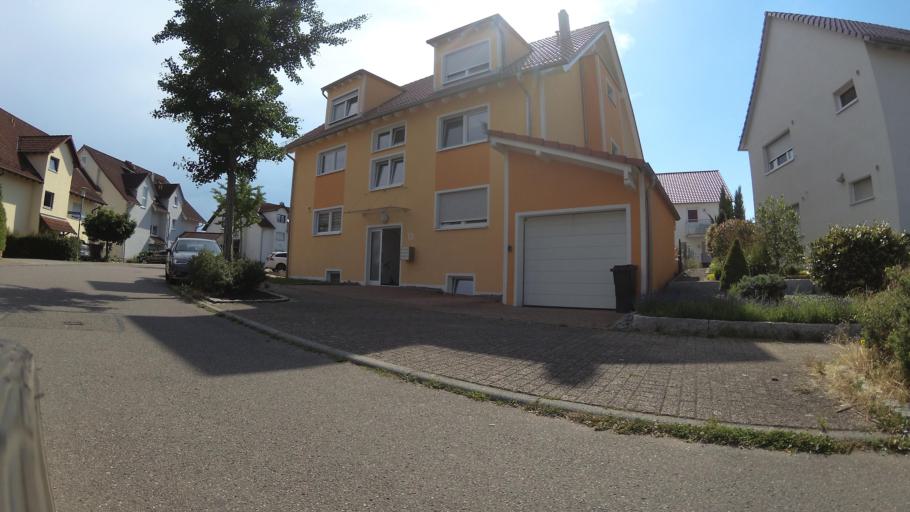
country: DE
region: Baden-Wuerttemberg
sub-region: Regierungsbezirk Stuttgart
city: Bad Rappenau
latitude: 49.2502
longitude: 9.1265
